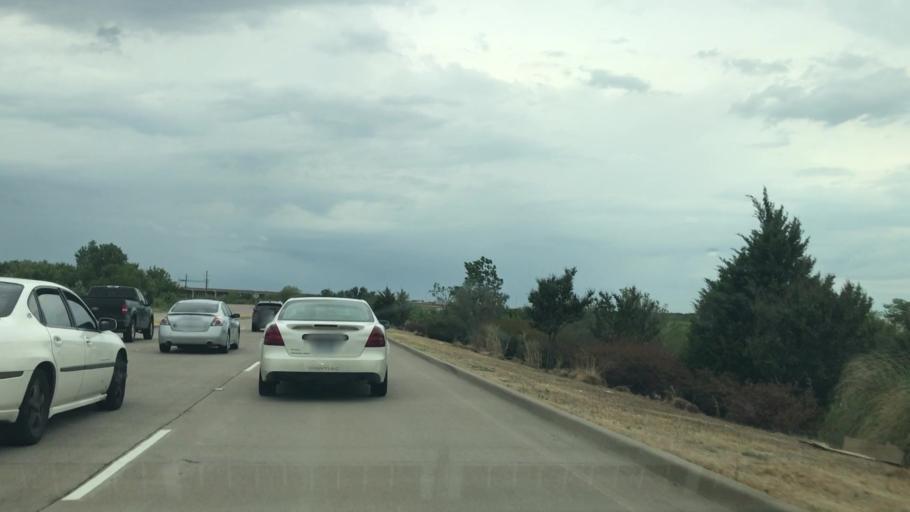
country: US
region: Texas
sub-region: Dallas County
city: Carrollton
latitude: 32.9624
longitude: -96.9228
